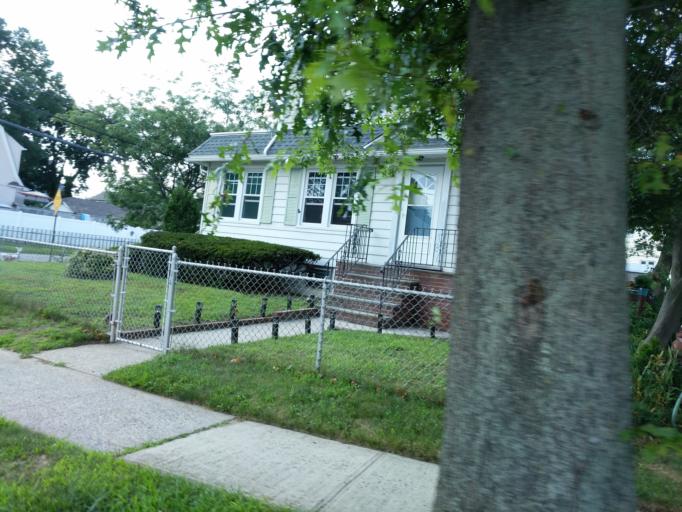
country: US
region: New York
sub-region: Nassau County
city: Hewlett
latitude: 40.6494
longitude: -73.7042
